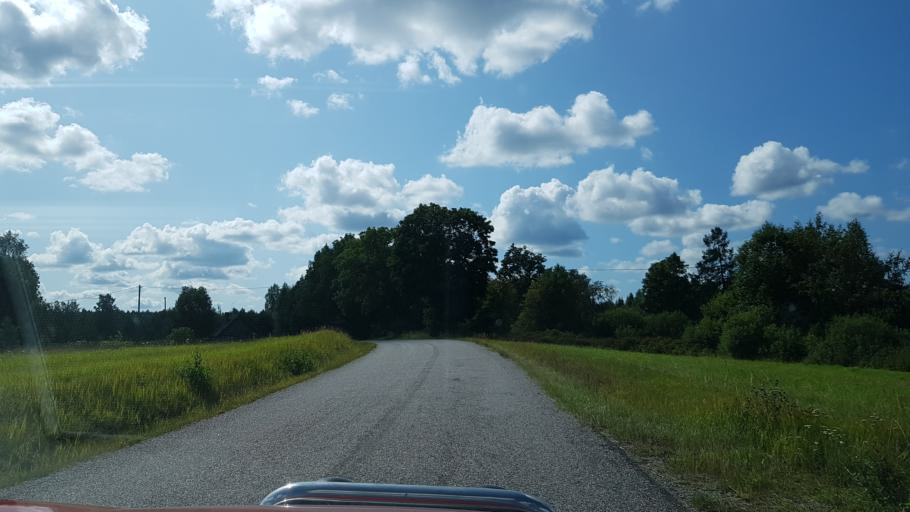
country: EE
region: Vorumaa
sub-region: Voru linn
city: Voru
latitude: 57.7232
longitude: 27.2093
